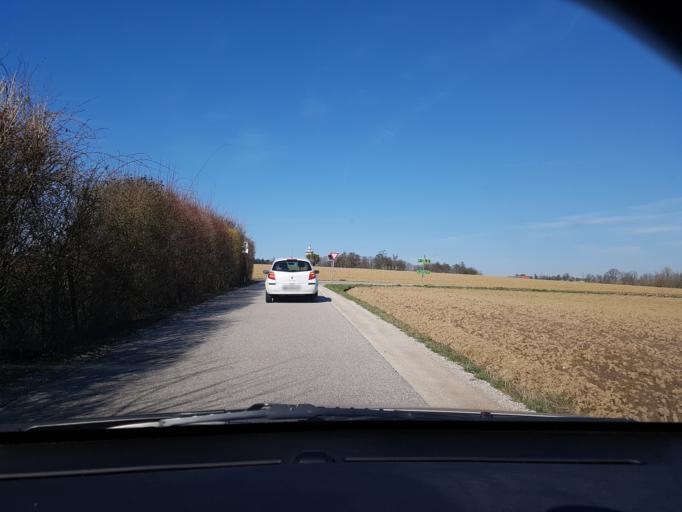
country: AT
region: Upper Austria
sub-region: Politischer Bezirk Linz-Land
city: Ansfelden
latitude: 48.1977
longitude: 14.3109
